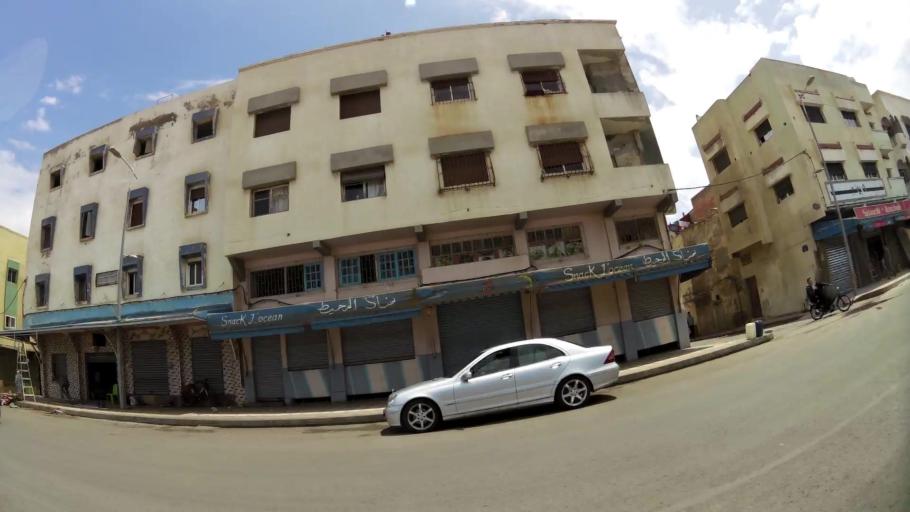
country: MA
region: Rabat-Sale-Zemmour-Zaer
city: Sale
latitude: 34.0532
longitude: -6.8231
